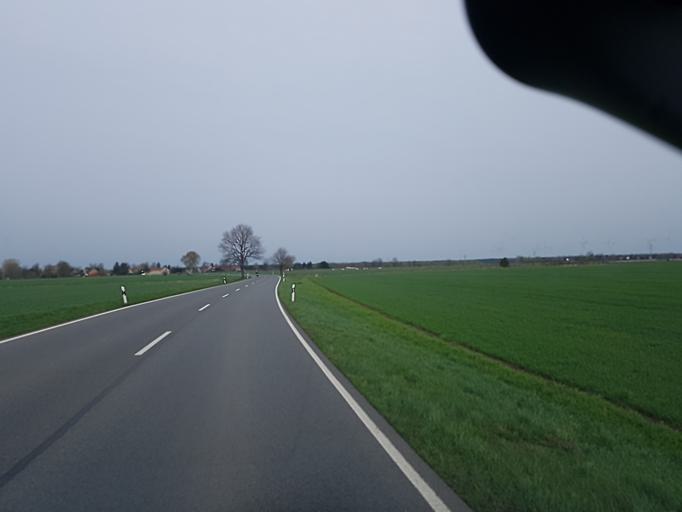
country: DE
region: Brandenburg
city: Falkenberg
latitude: 51.5350
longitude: 13.2890
